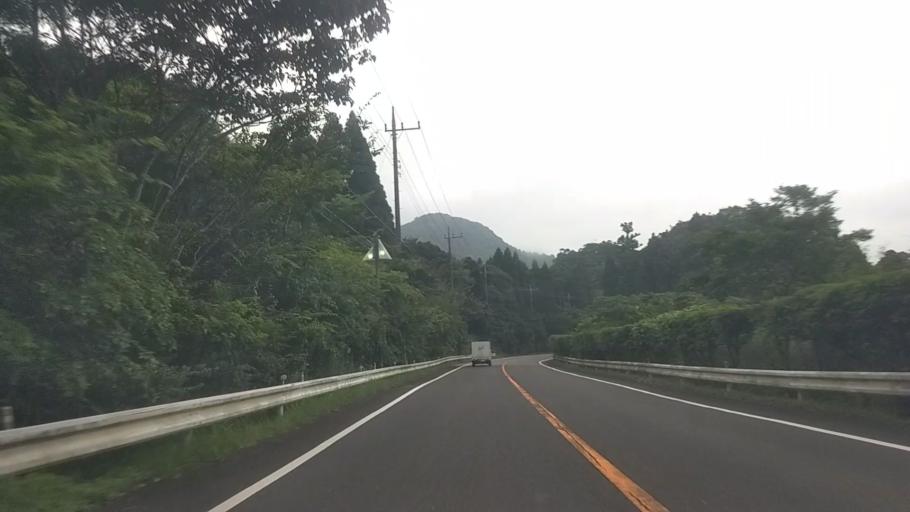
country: JP
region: Chiba
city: Kawaguchi
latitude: 35.1496
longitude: 140.0678
